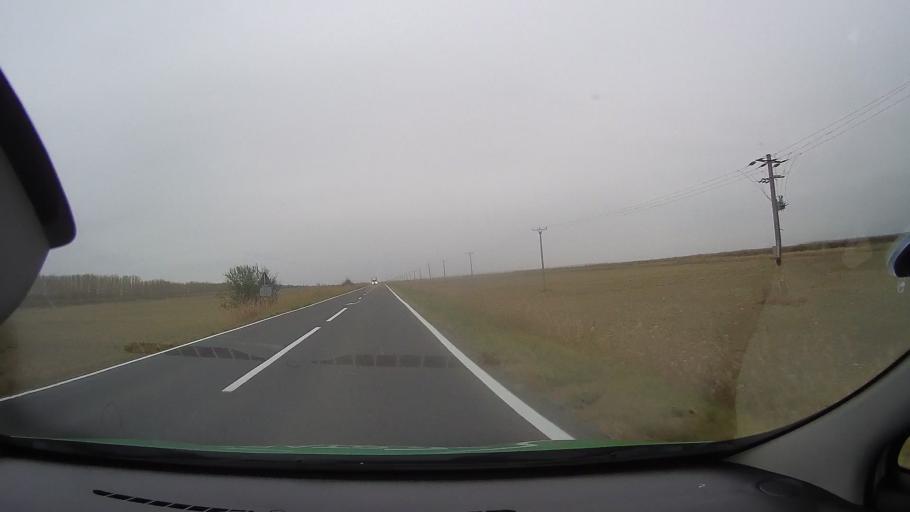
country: RO
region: Ialomita
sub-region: Comuna Giurgeni
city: Giurgeni
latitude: 44.7224
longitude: 27.8529
